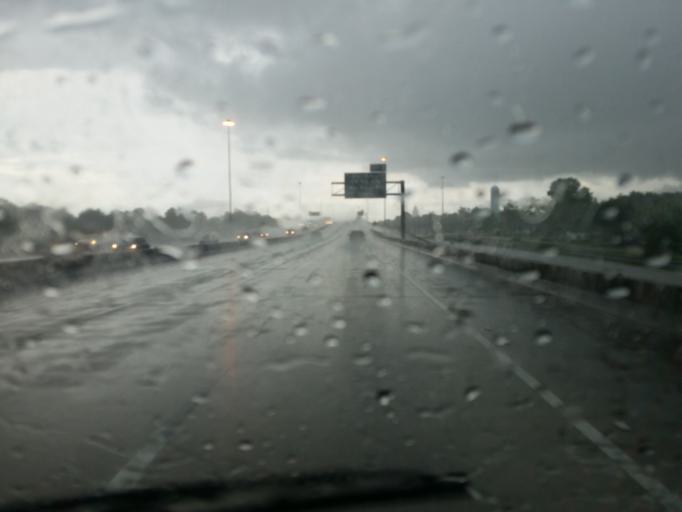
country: US
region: Alabama
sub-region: Mobile County
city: Prichard
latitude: 30.7379
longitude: -88.0852
